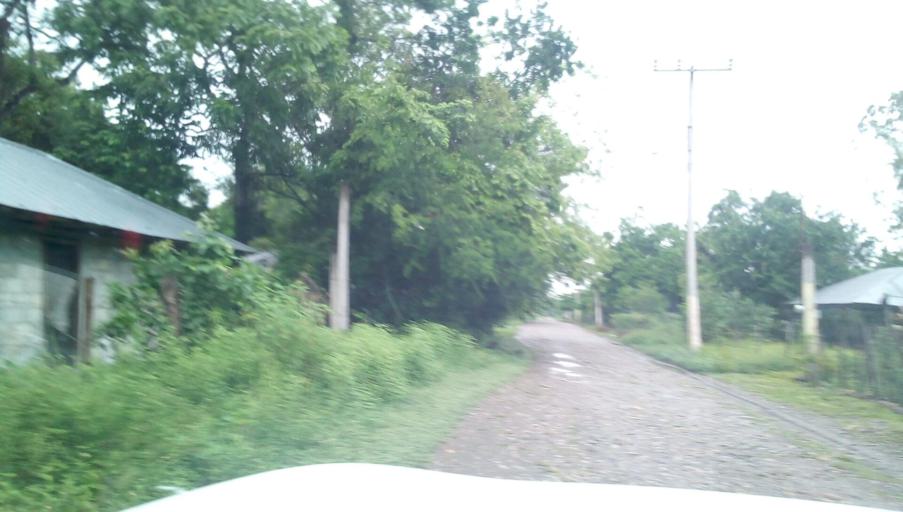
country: MX
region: Veracruz
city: Tempoal de Sanchez
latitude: 21.4181
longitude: -98.4245
